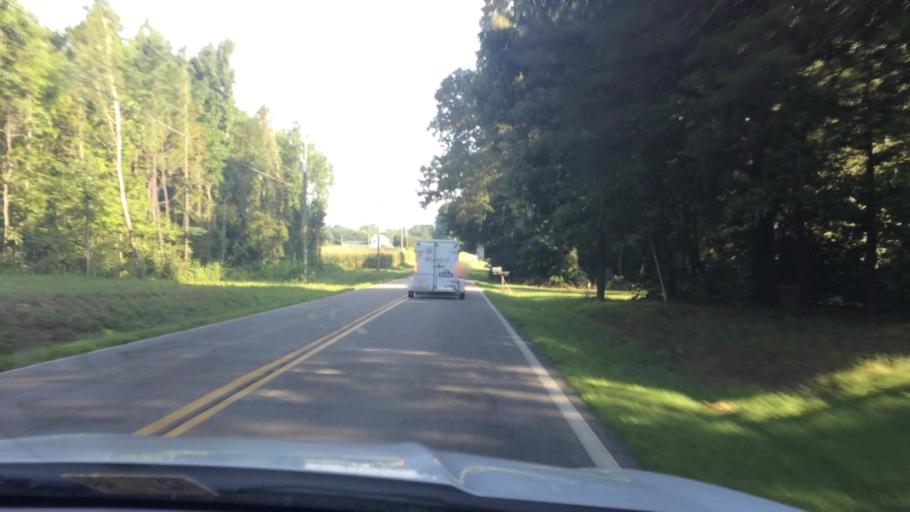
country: US
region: Virginia
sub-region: Middlesex County
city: Deltaville
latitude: 37.5742
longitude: -76.4550
